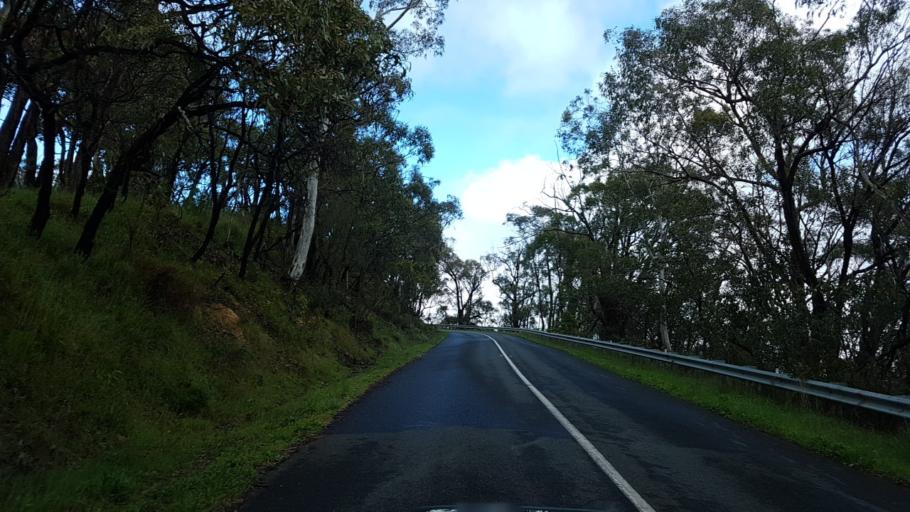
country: AU
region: South Australia
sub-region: Adelaide Hills
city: Adelaide Hills
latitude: -34.9078
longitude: 138.7632
